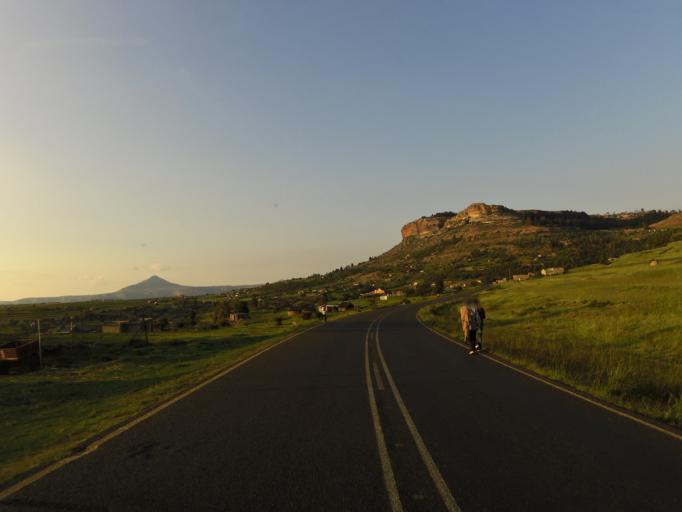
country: LS
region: Leribe
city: Leribe
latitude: -28.9617
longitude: 28.1714
